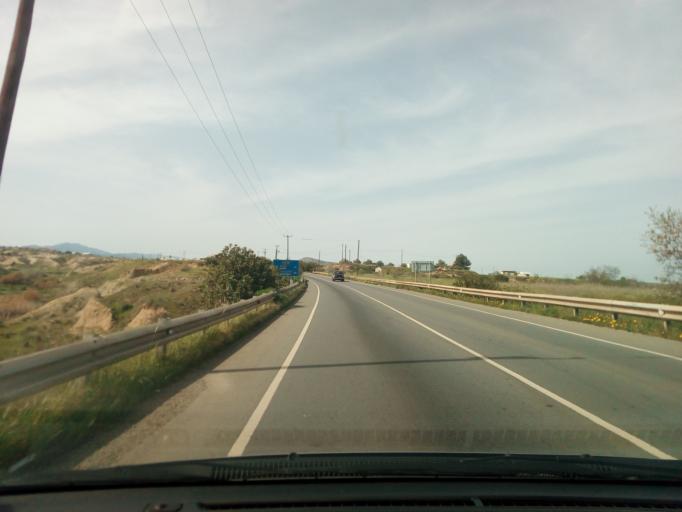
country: CY
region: Lefkosia
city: Arediou
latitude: 35.0524
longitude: 33.1958
